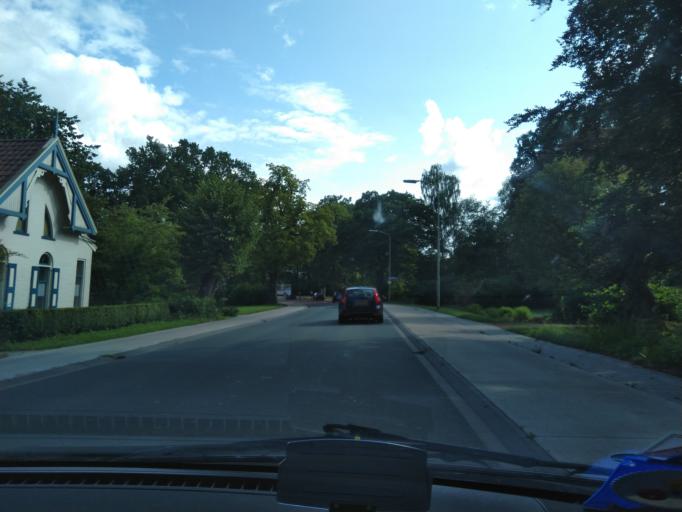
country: NL
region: Groningen
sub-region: Gemeente Haren
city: Haren
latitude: 53.1540
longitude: 6.5650
